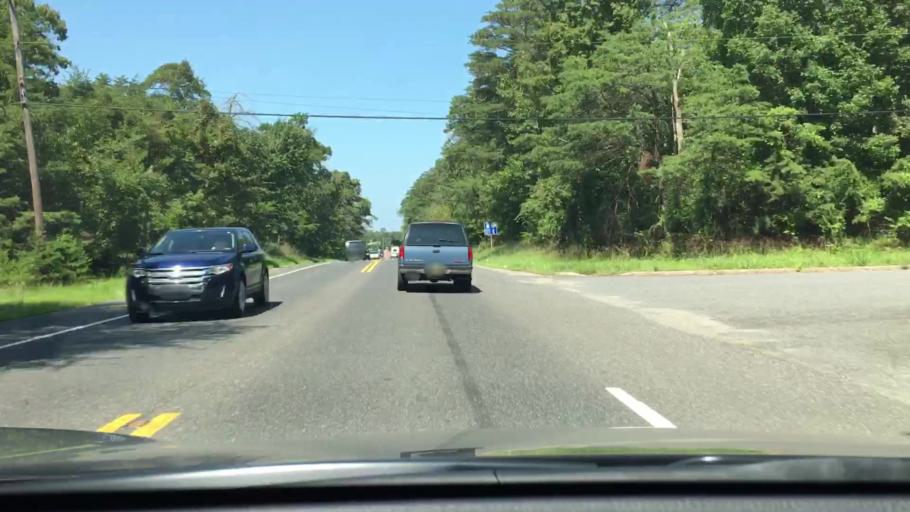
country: US
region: New Jersey
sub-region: Cumberland County
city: Port Norris
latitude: 39.2887
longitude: -74.9617
